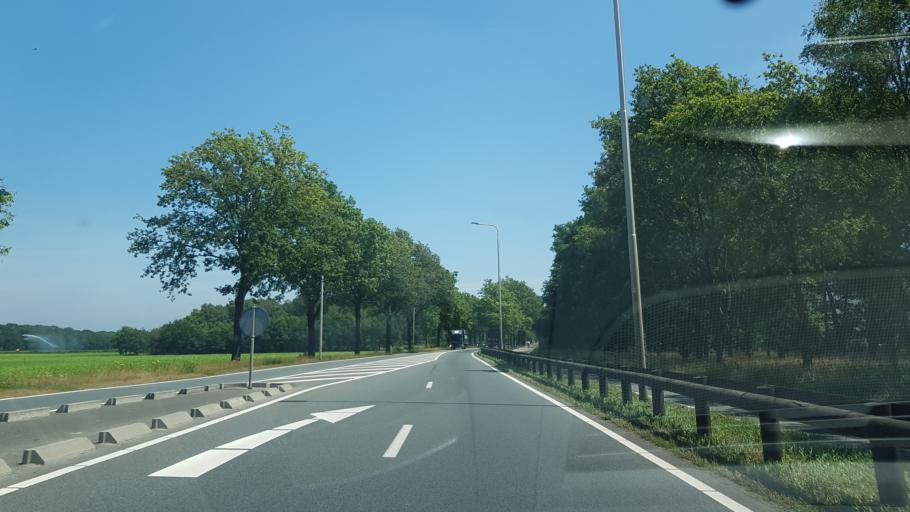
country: NL
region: North Brabant
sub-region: Gemeente Helmond
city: Helmond
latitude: 51.4698
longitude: 5.7266
